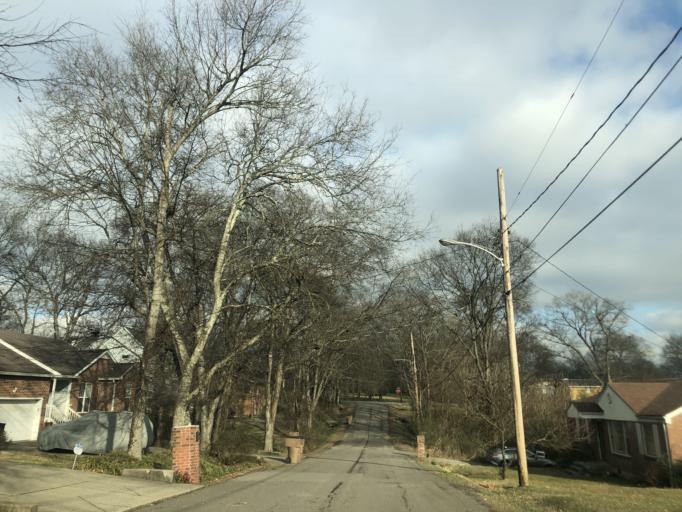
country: US
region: Tennessee
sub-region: Davidson County
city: Nashville
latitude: 36.2045
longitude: -86.7883
